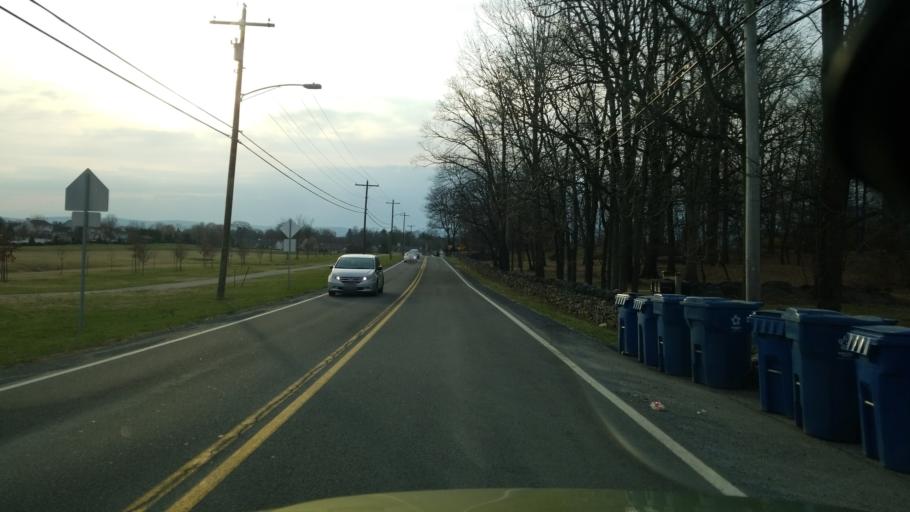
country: US
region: Virginia
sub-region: Clarke County
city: Berryville
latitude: 39.1600
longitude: -77.9940
